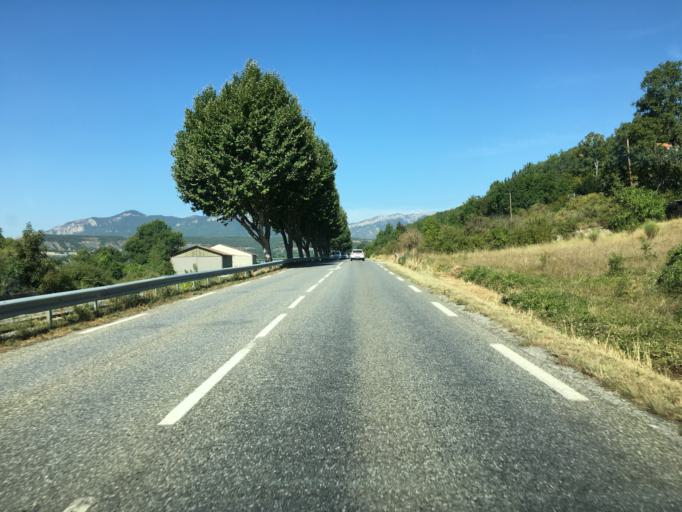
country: FR
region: Provence-Alpes-Cote d'Azur
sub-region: Departement des Hautes-Alpes
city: Laragne-Monteglin
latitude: 44.3195
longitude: 5.8083
